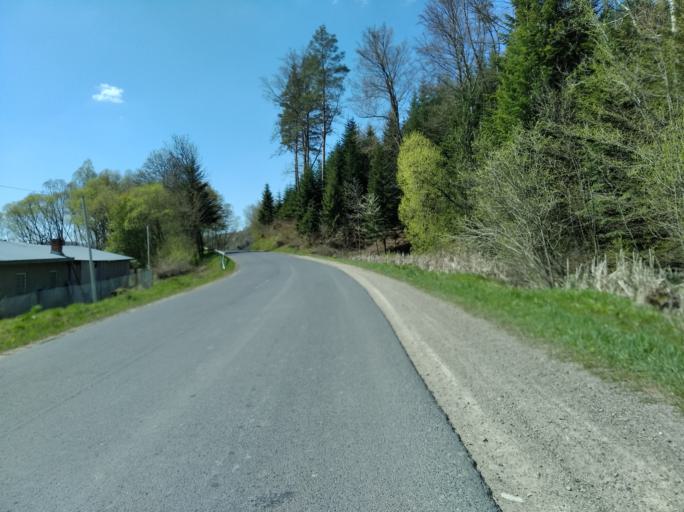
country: PL
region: Subcarpathian Voivodeship
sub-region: Powiat brzozowski
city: Dydnia
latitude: 49.7125
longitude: 22.2027
